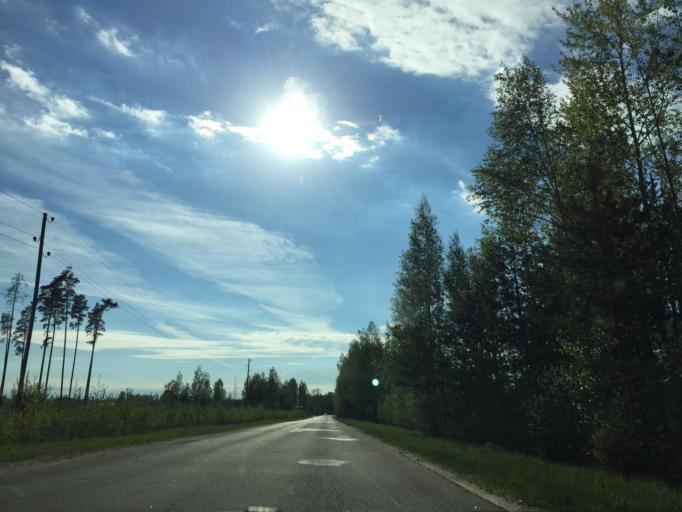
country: LV
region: Lecava
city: Iecava
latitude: 56.6908
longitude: 24.1007
